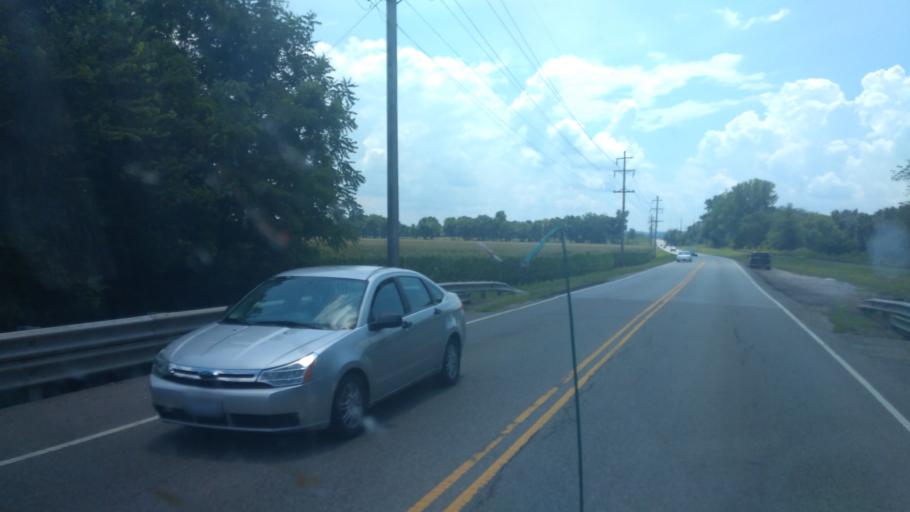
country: US
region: Ohio
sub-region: Fairfield County
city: Lancaster
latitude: 39.7442
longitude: -82.6577
